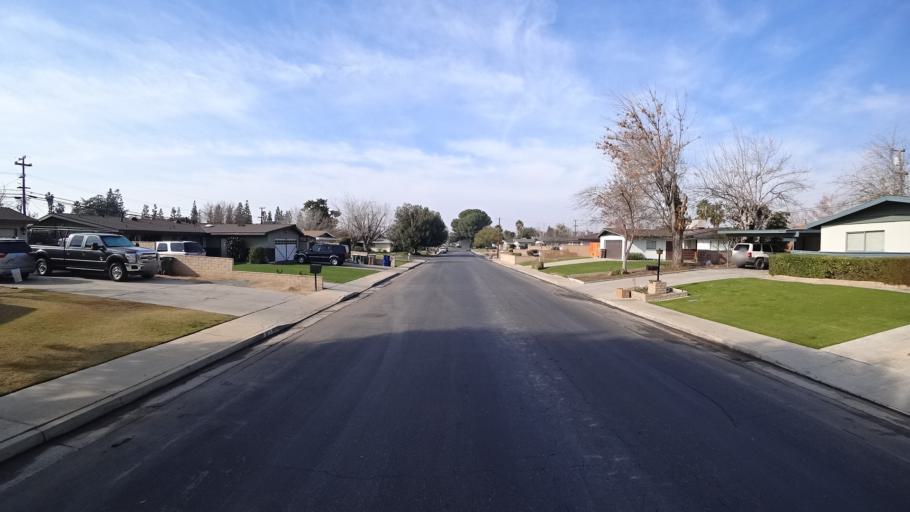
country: US
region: California
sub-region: Kern County
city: Oildale
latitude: 35.3998
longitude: -118.9637
